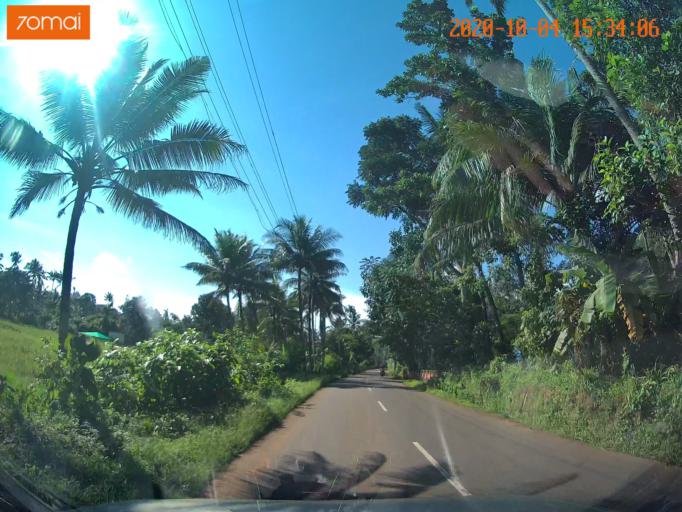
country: IN
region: Kerala
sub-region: Kottayam
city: Palackattumala
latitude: 9.7351
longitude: 76.6237
